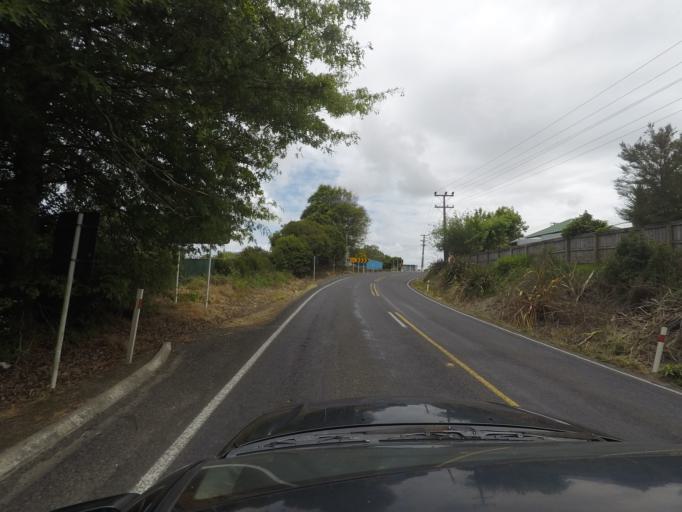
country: NZ
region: Auckland
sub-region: Auckland
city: Parakai
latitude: -36.6256
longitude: 174.5021
